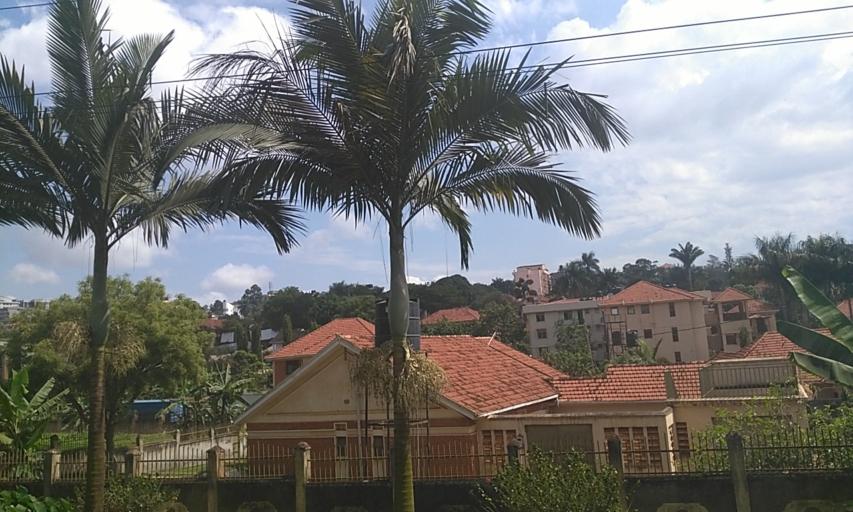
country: UG
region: Central Region
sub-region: Wakiso District
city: Kireka
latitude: 0.3467
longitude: 32.6127
